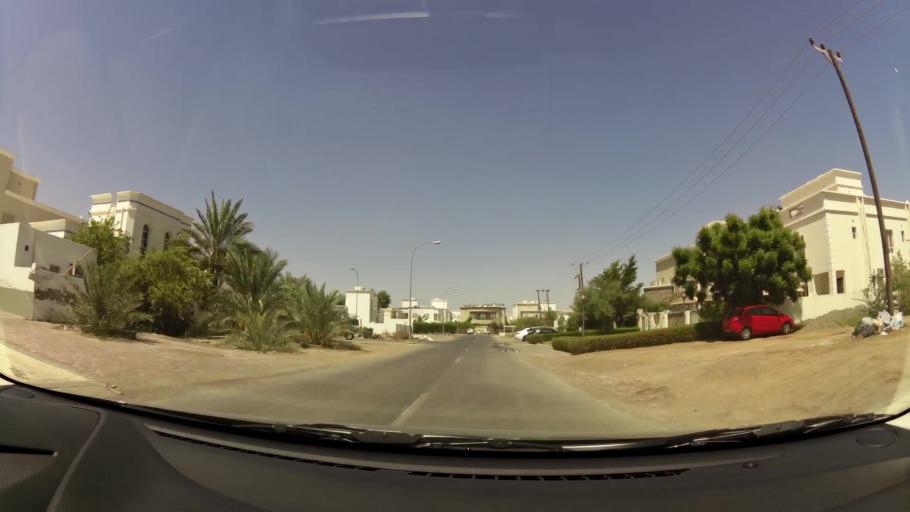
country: OM
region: Muhafazat Masqat
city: As Sib al Jadidah
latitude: 23.6220
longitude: 58.2567
